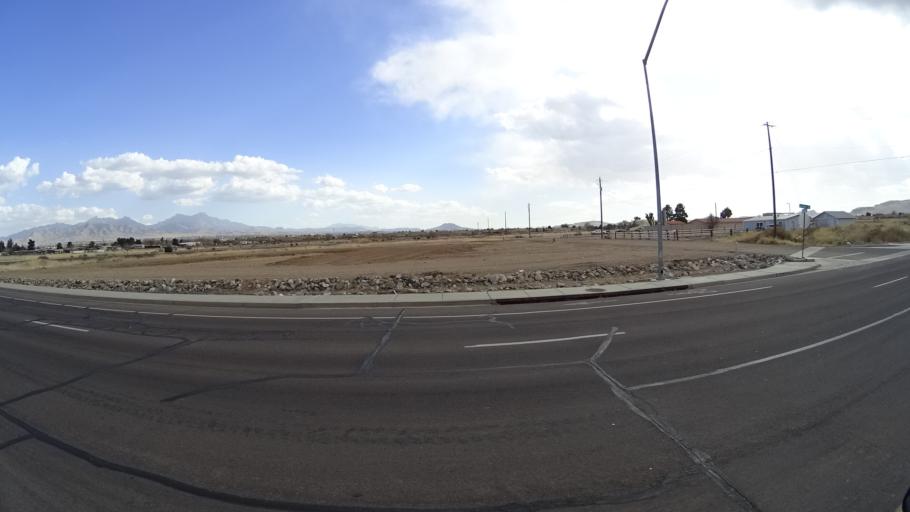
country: US
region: Arizona
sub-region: Mohave County
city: New Kingman-Butler
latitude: 35.2395
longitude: -114.0232
